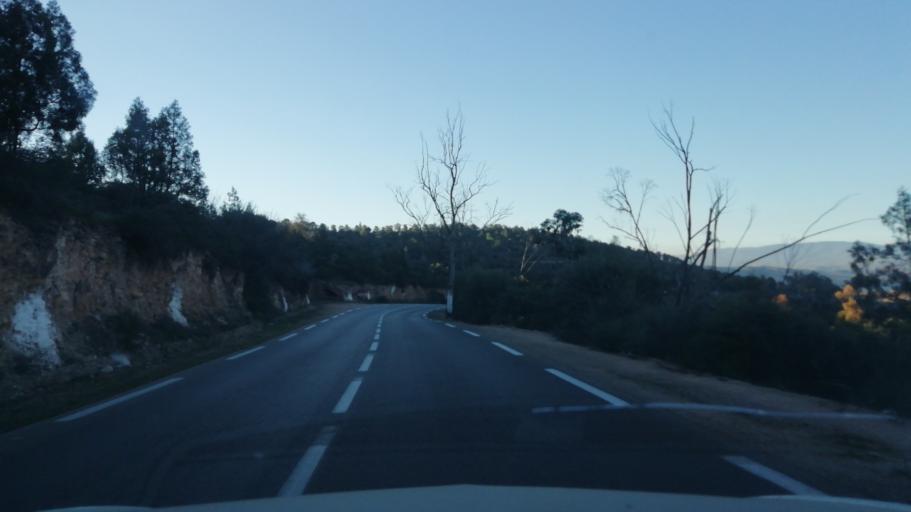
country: DZ
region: Tlemcen
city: Beni Mester
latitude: 34.8166
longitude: -1.6339
